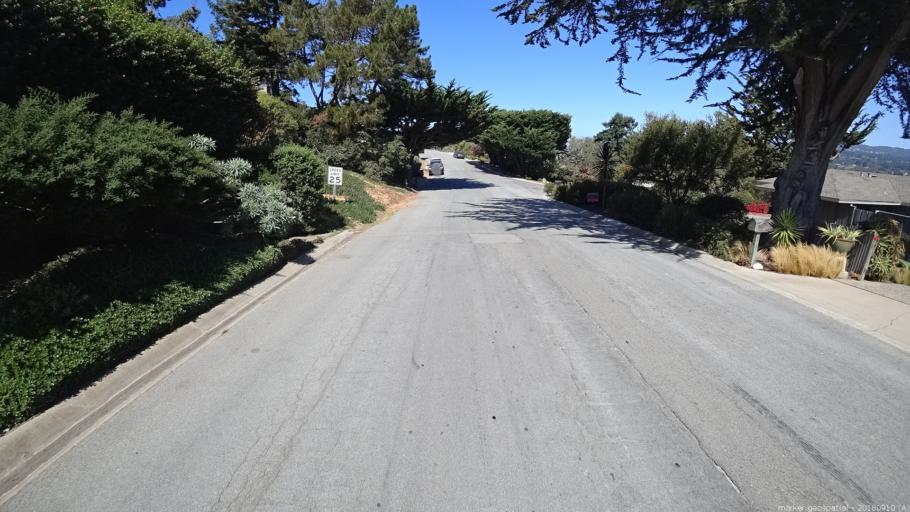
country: US
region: California
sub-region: Monterey County
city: Carmel-by-the-Sea
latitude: 36.5309
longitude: -121.9210
